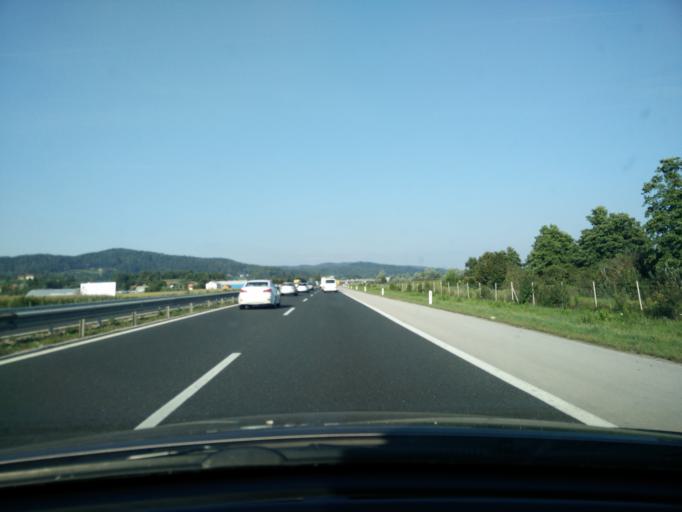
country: SI
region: Vrhnika
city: Verd
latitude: 45.9875
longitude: 14.3216
